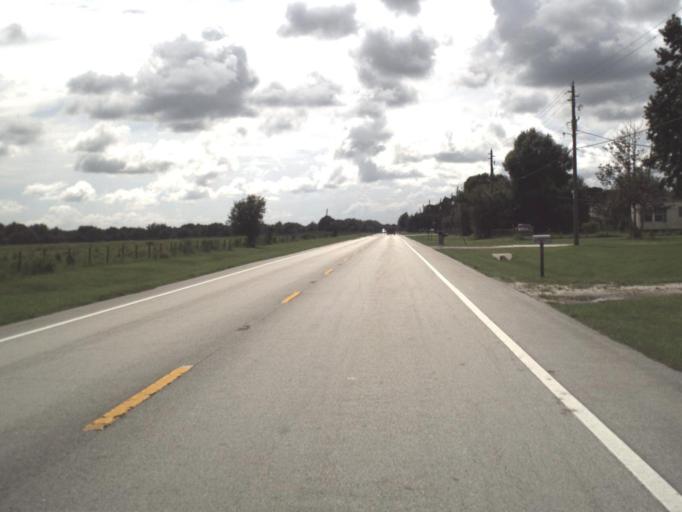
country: US
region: Florida
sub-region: DeSoto County
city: Arcadia
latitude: 27.2108
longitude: -81.9143
